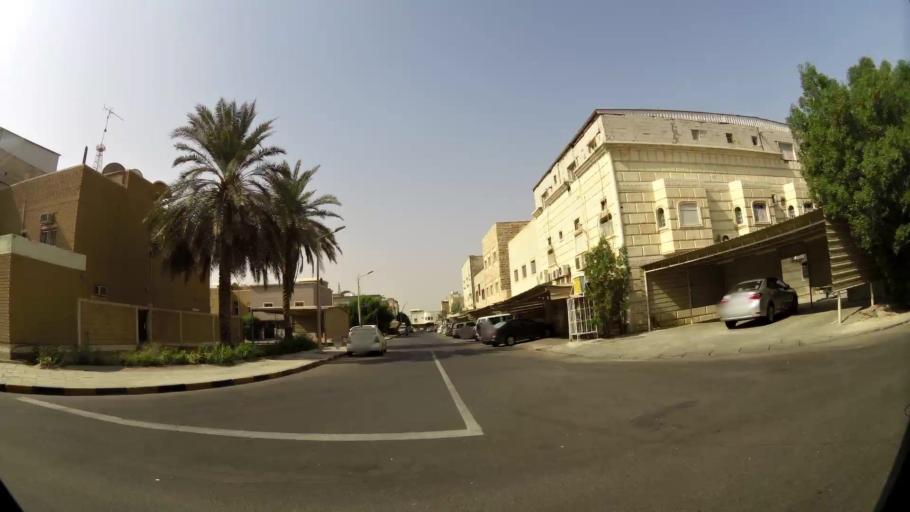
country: KW
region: Al Asimah
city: Ar Rabiyah
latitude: 29.2859
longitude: 47.8932
